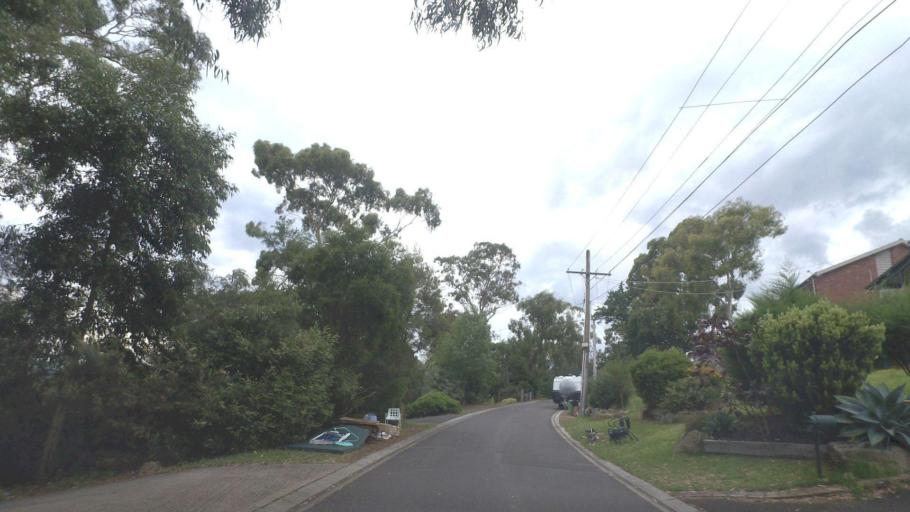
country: AU
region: Victoria
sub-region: Yarra Ranges
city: Lilydale
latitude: -37.7602
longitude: 145.3658
